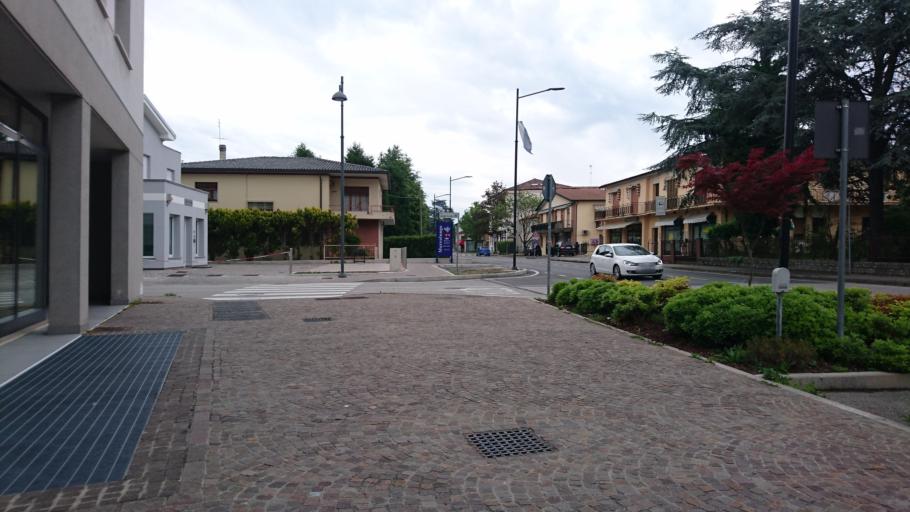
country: IT
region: Veneto
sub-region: Provincia di Padova
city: Selvazzano Dentro
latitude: 45.3937
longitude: 11.7802
